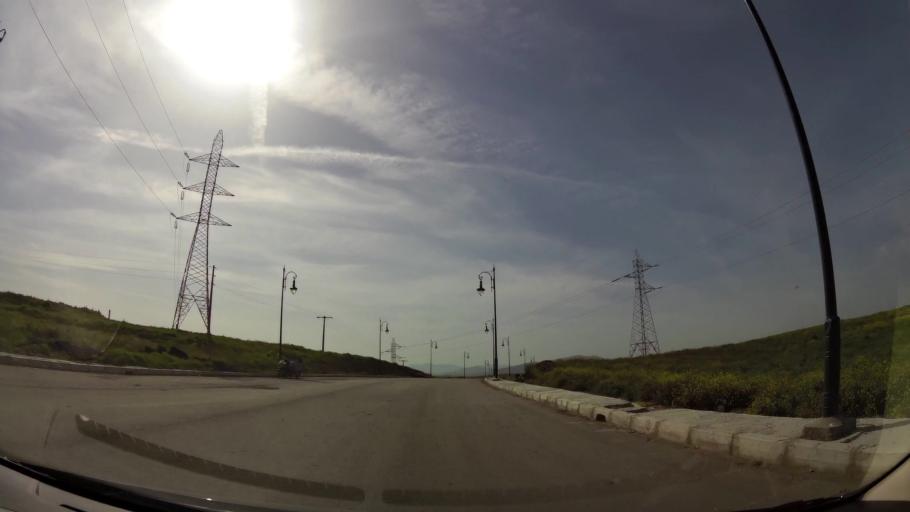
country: MA
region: Tanger-Tetouan
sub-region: Tanger-Assilah
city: Tangier
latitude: 35.7050
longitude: -5.8125
